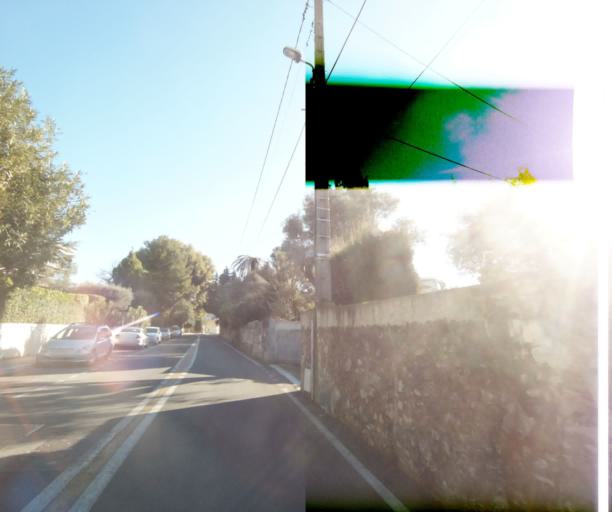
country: FR
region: Provence-Alpes-Cote d'Azur
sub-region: Departement des Alpes-Maritimes
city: Antibes
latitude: 43.5786
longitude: 7.1106
